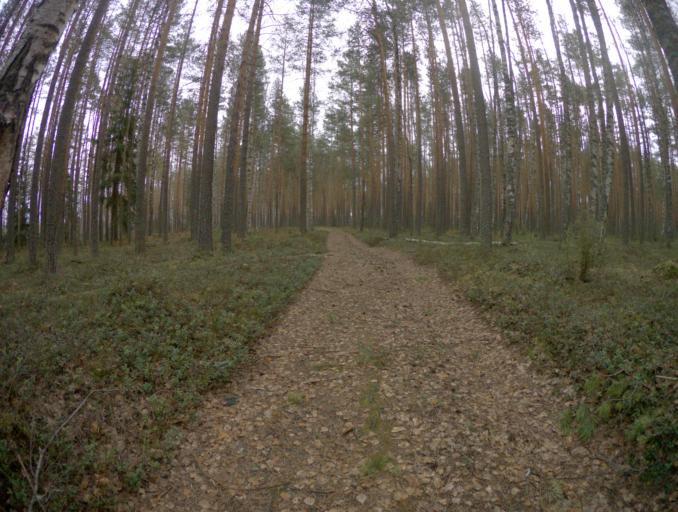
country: RU
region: Vladimir
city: Raduzhnyy
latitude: 55.9470
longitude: 40.2872
